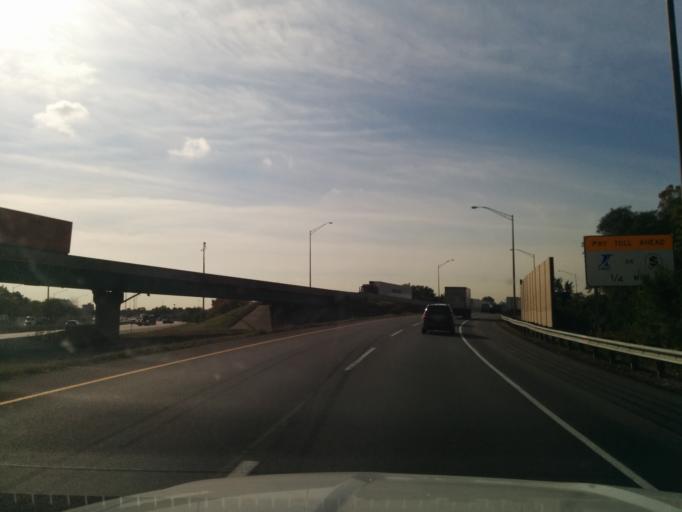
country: US
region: Illinois
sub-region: Cook County
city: Indian Head Park
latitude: 41.7709
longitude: -87.9070
